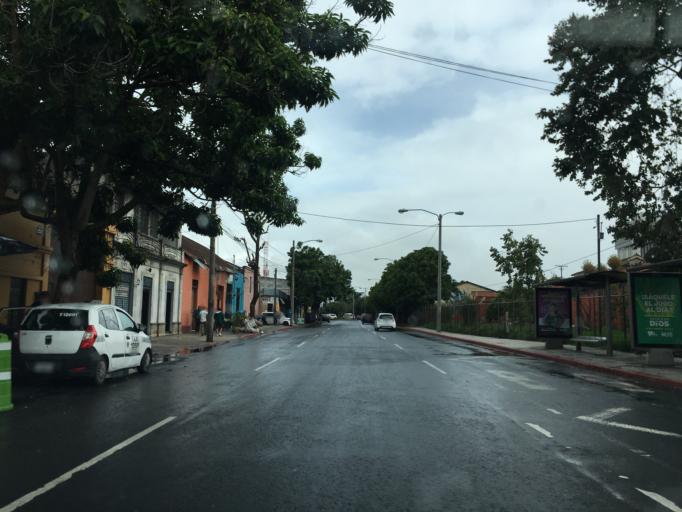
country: GT
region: Guatemala
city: Guatemala City
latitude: 14.6299
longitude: -90.5110
